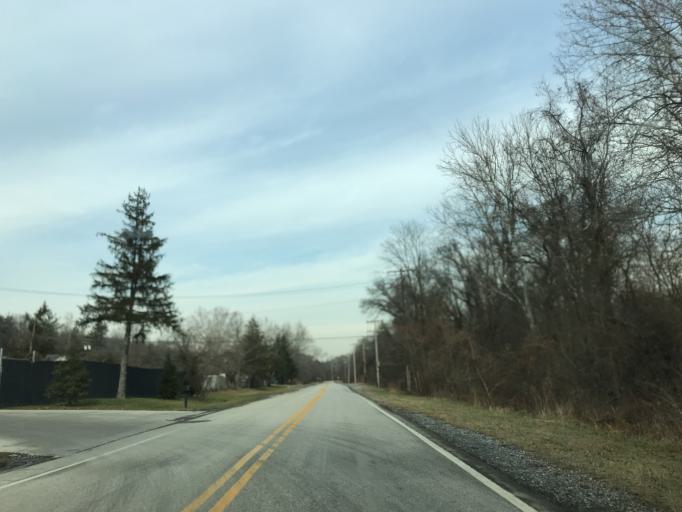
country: US
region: Maryland
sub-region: Howard County
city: Hanover
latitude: 39.1944
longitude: -76.7146
